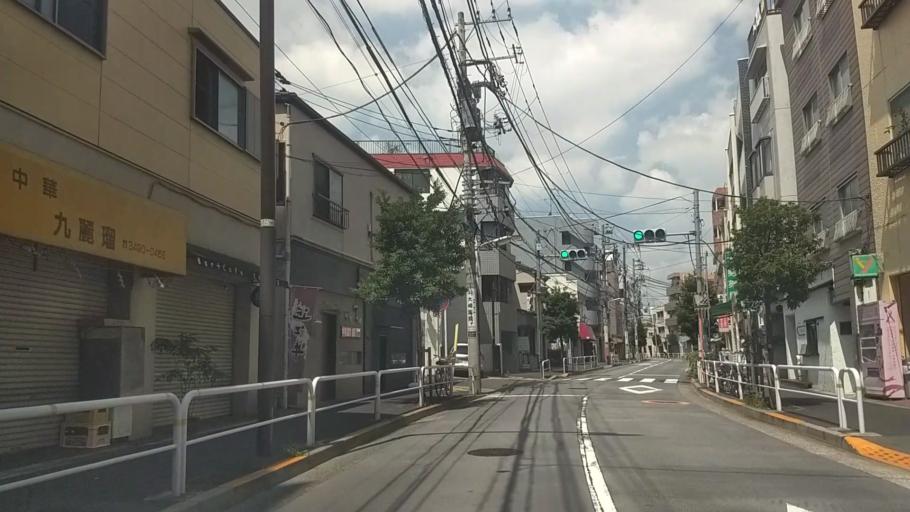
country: JP
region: Tokyo
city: Tokyo
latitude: 35.6164
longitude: 139.7262
